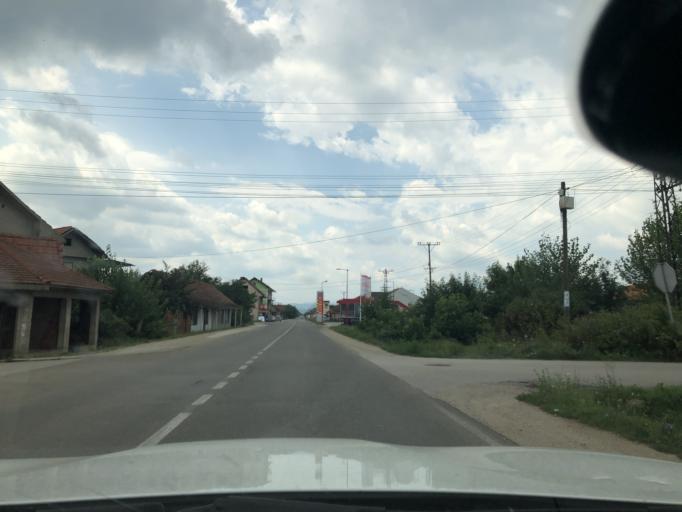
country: RS
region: Central Serbia
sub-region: Jablanicki Okrug
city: Lebane
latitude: 42.9628
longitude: 21.8377
